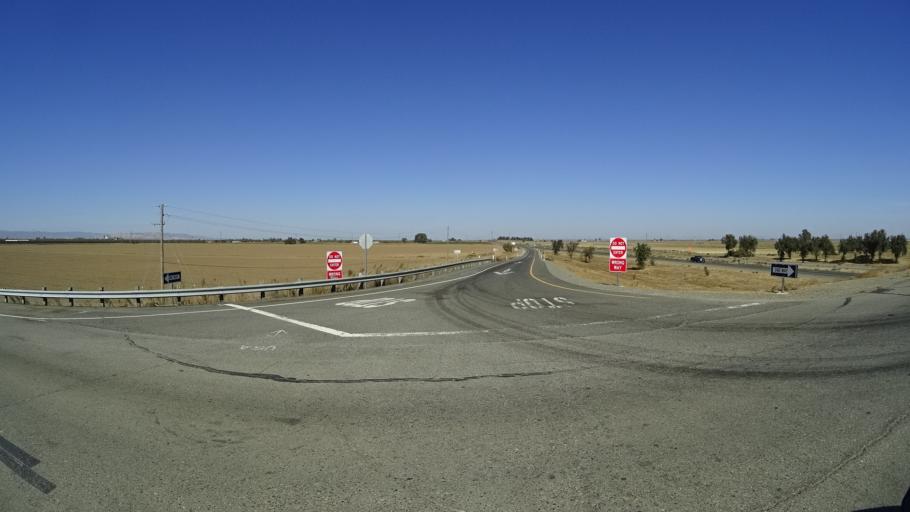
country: US
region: California
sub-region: Yolo County
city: Cottonwood
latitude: 38.6203
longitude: -121.9547
